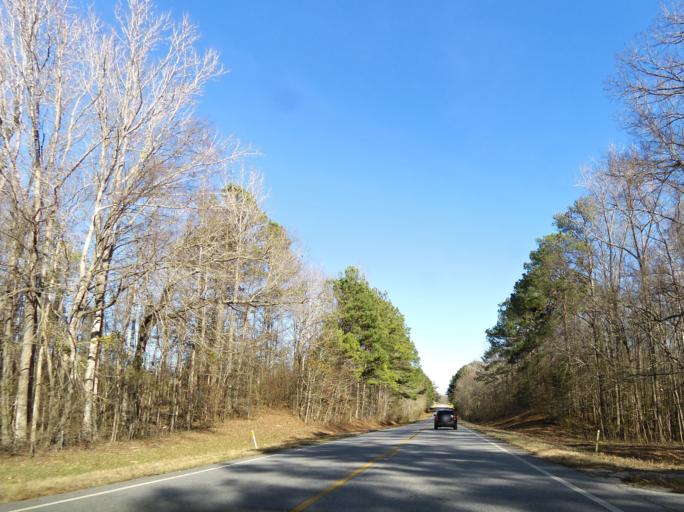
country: US
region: Georgia
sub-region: Crawford County
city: Roberta
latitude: 32.7585
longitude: -84.1227
